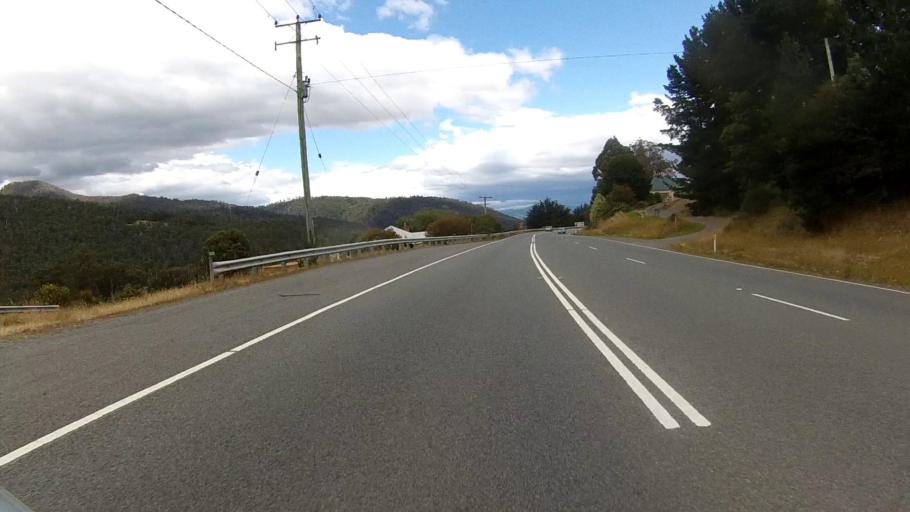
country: AU
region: Tasmania
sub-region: Huon Valley
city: Huonville
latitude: -42.9766
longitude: 147.1439
